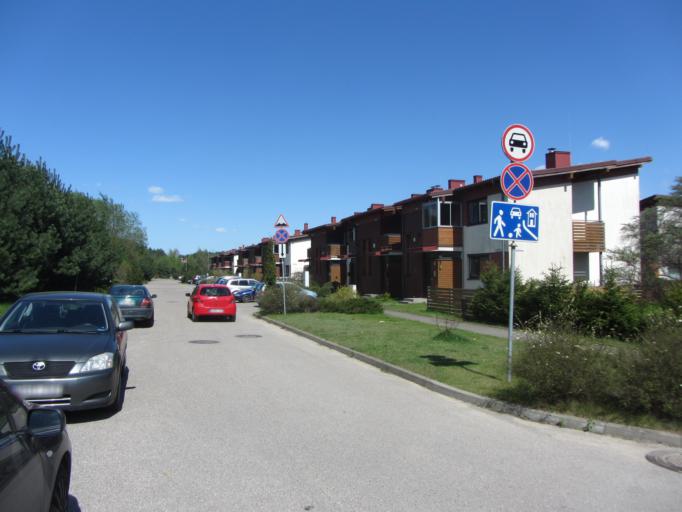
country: LT
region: Vilnius County
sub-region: Vilnius
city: Fabijoniskes
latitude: 54.7529
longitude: 25.2858
